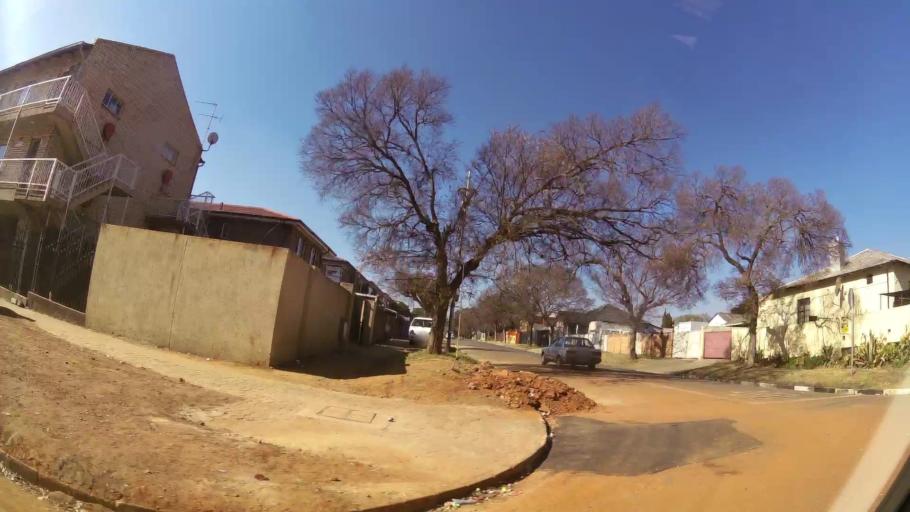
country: ZA
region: Gauteng
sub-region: City of Johannesburg Metropolitan Municipality
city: Johannesburg
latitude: -26.2570
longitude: 28.0394
